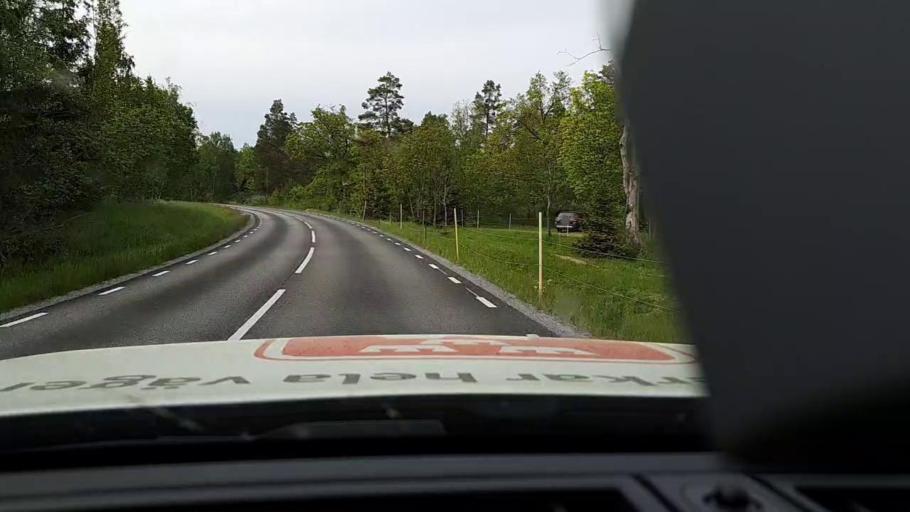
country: SE
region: Stockholm
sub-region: Haninge Kommun
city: Haninge
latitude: 59.1146
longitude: 18.1905
